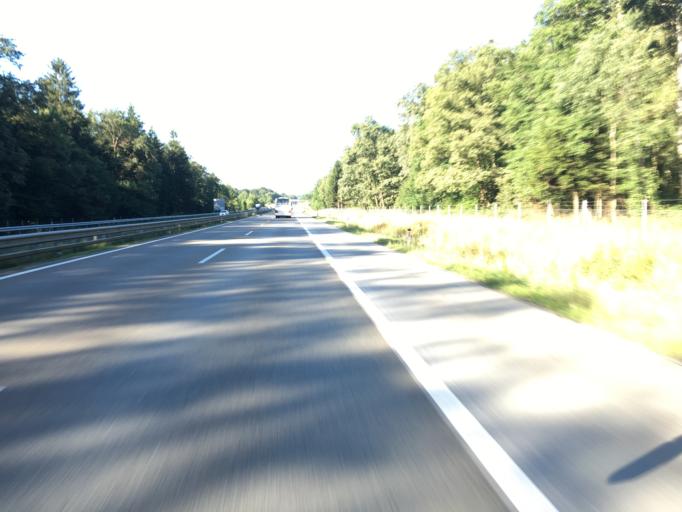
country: SI
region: Race-Fram
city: Fram
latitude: 46.4418
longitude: 15.6443
